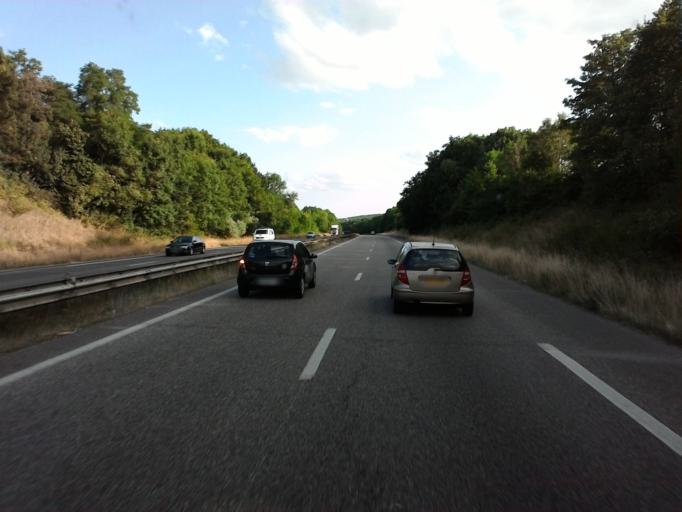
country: FR
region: Lorraine
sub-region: Departement de Meurthe-et-Moselle
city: Richardmenil
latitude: 48.6008
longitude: 6.1721
